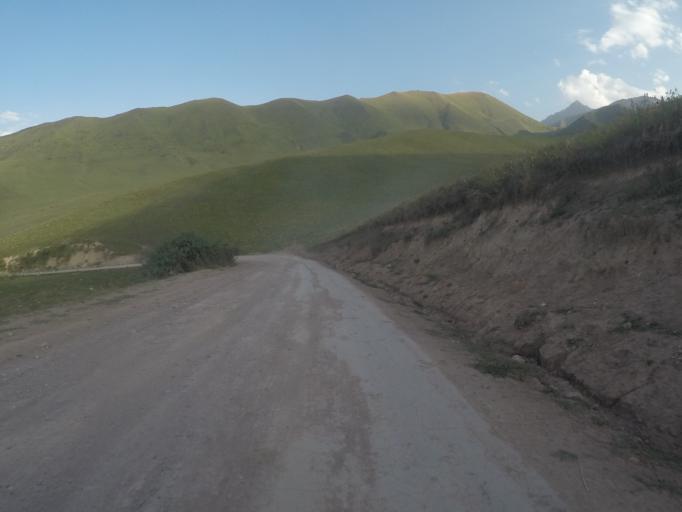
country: KG
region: Chuy
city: Bishkek
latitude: 42.6407
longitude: 74.6351
